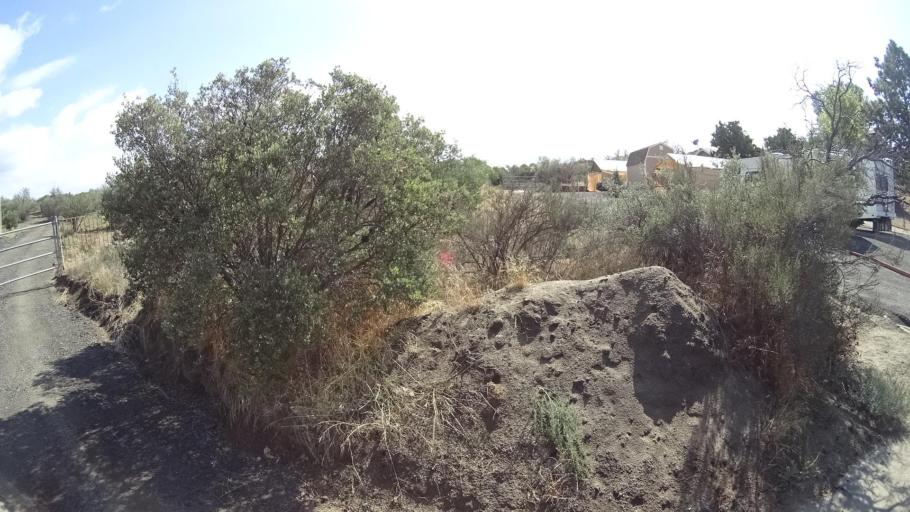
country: US
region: California
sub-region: San Diego County
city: Campo
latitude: 32.6779
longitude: -116.5010
